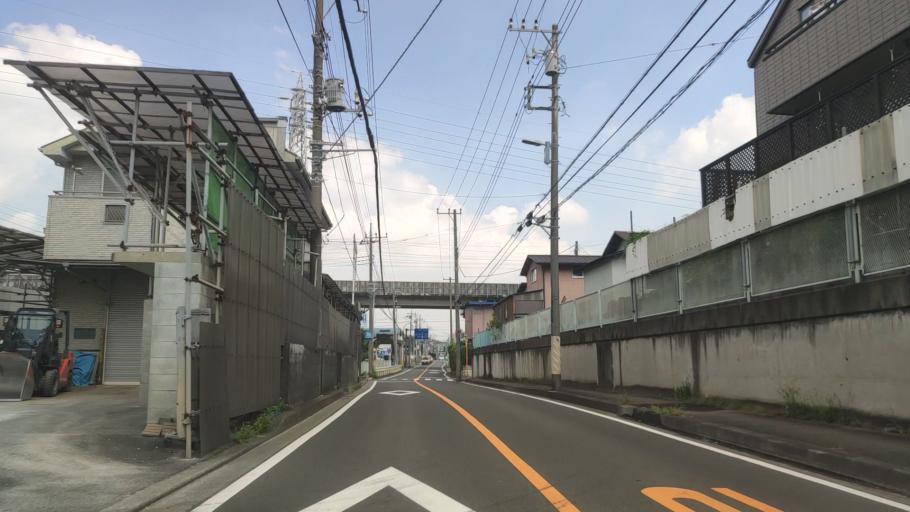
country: JP
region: Kanagawa
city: Minami-rinkan
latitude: 35.4455
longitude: 139.5051
